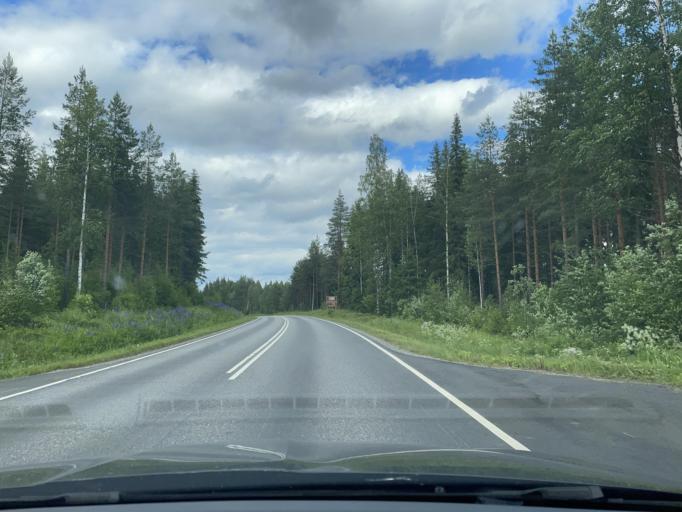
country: FI
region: Central Finland
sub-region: Jyvaeskylae
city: Petaejaevesi
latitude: 62.2194
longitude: 25.1566
